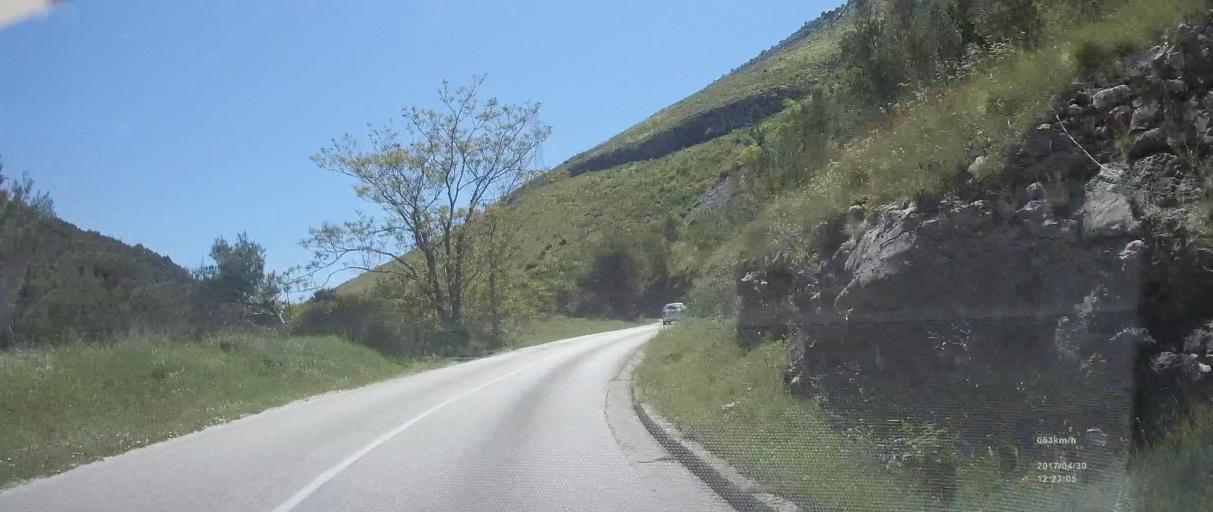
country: HR
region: Splitsko-Dalmatinska
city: Zrnovnica
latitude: 43.5178
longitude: 16.5755
